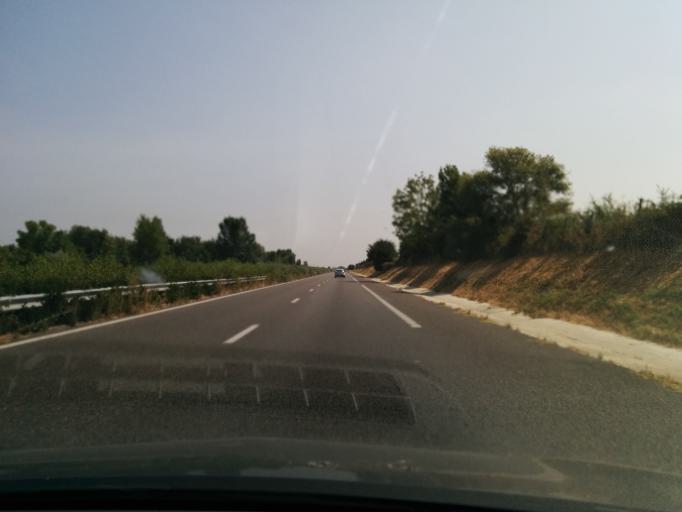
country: FR
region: Midi-Pyrenees
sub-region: Departement du Tarn
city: Giroussens
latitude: 43.7962
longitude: 1.7630
